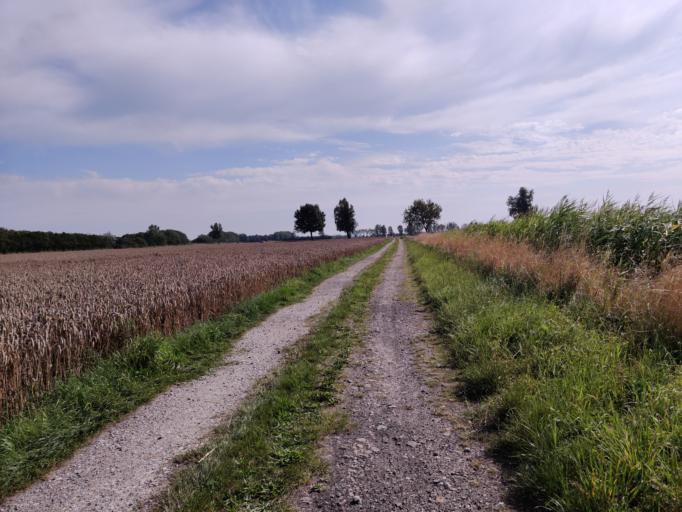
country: DK
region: Zealand
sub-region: Guldborgsund Kommune
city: Nykobing Falster
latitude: 54.6791
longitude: 11.9095
